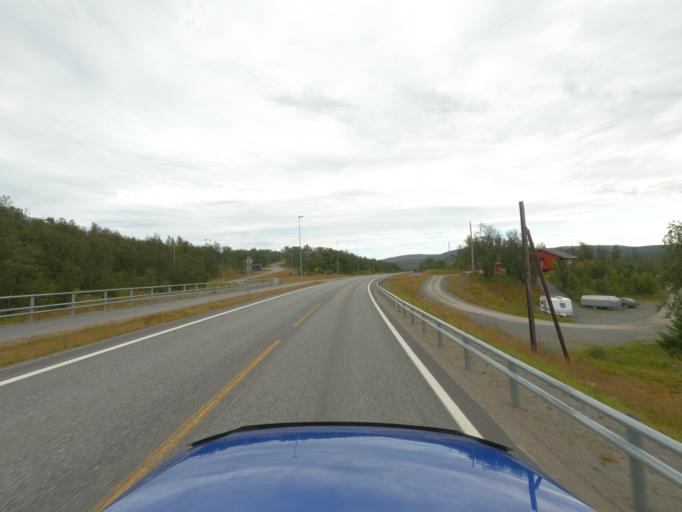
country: NO
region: Finnmark Fylke
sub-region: Kvalsund
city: Kvalsund
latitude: 70.4411
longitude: 24.4715
